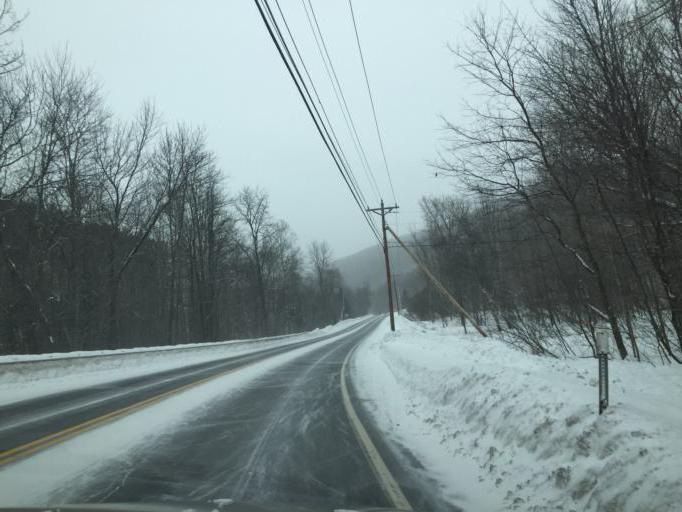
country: US
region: New Hampshire
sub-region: Carroll County
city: North Conway
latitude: 44.1836
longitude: -71.2284
